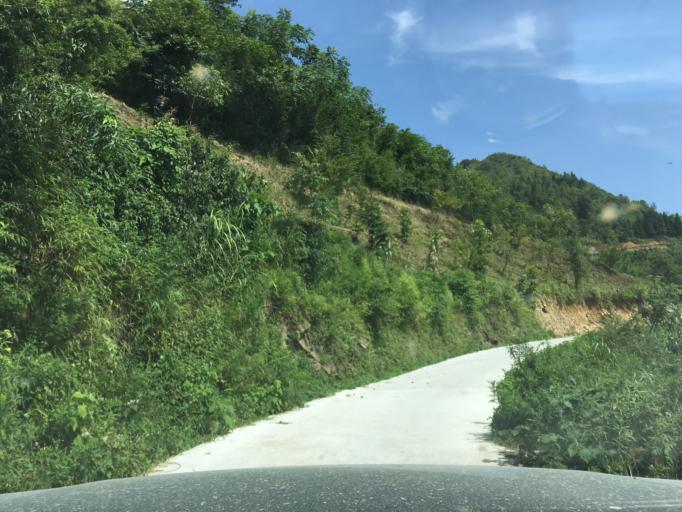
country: CN
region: Guangxi Zhuangzu Zizhiqu
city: Xinzhou
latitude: 24.9665
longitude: 105.6205
